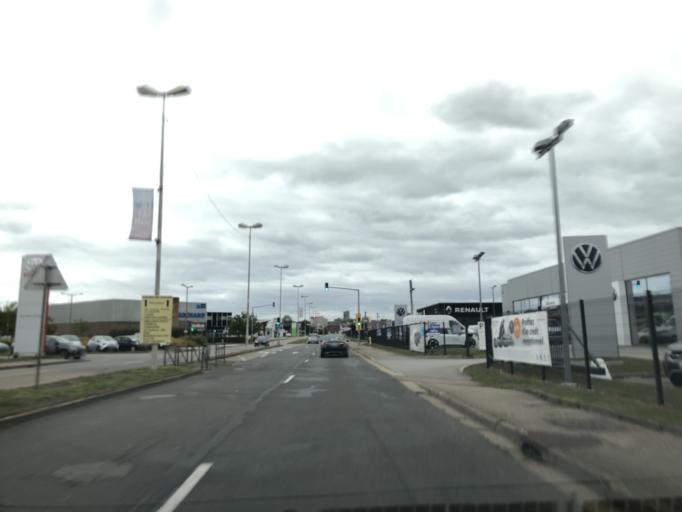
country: FR
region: Haute-Normandie
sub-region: Departement de la Seine-Maritime
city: Rouxmesnil-Bouteilles
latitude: 49.9175
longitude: 1.0883
